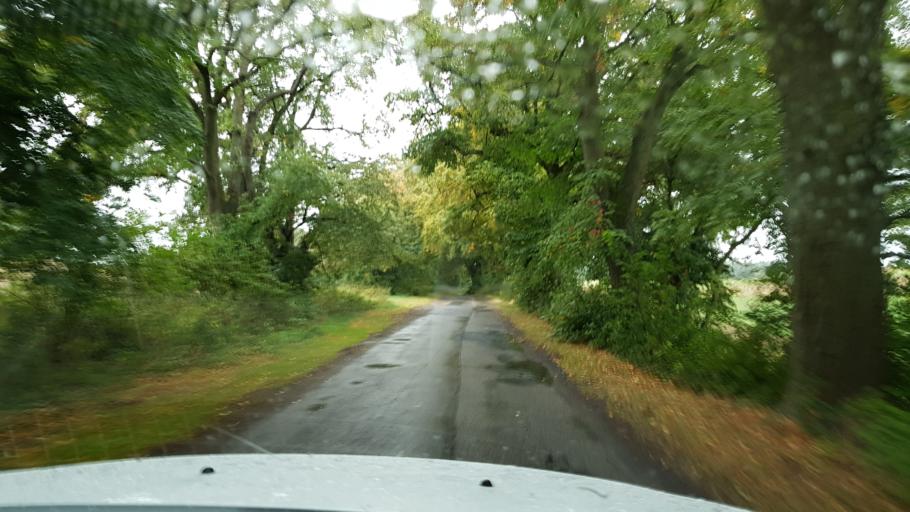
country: DE
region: Brandenburg
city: Schwedt (Oder)
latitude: 52.9975
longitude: 14.2786
